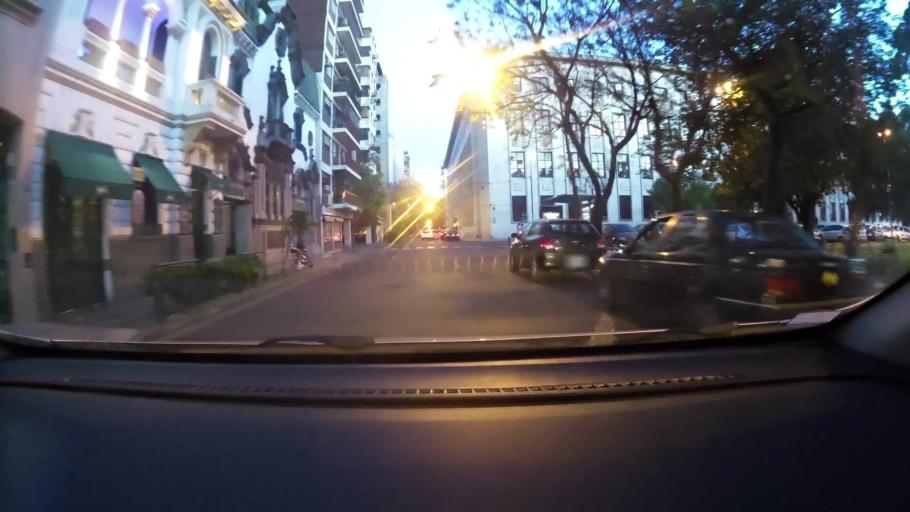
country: AR
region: Santa Fe
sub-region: Departamento de Rosario
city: Rosario
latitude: -32.9536
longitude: -60.6548
